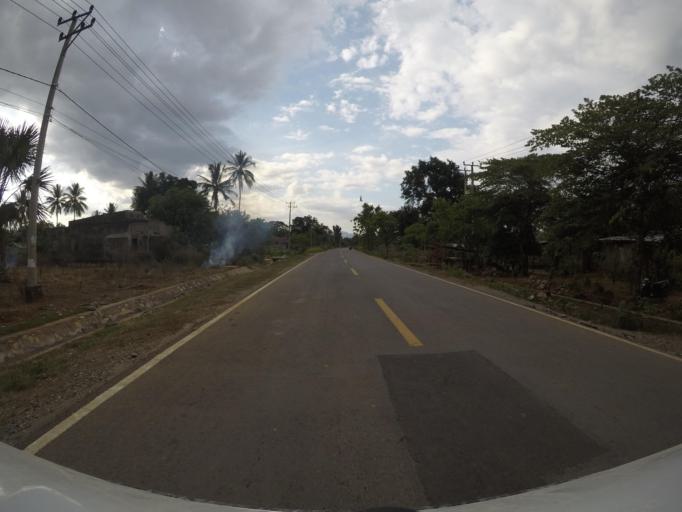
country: TL
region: Bobonaro
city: Maliana
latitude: -8.9685
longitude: 125.2178
